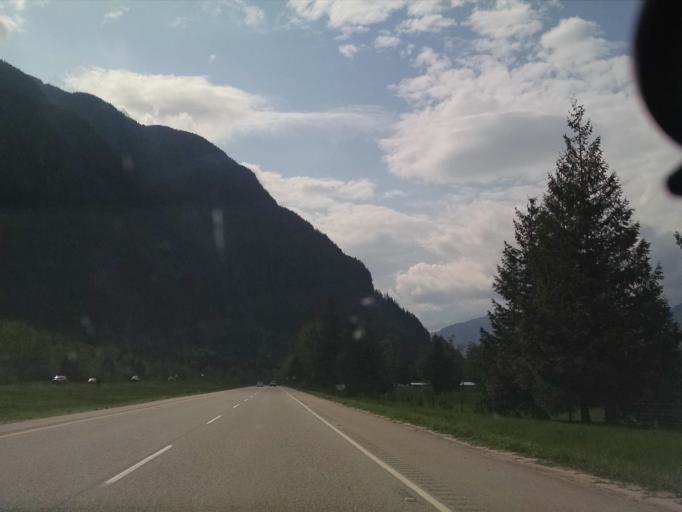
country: CA
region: British Columbia
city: Hope
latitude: 49.3628
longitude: -121.5029
